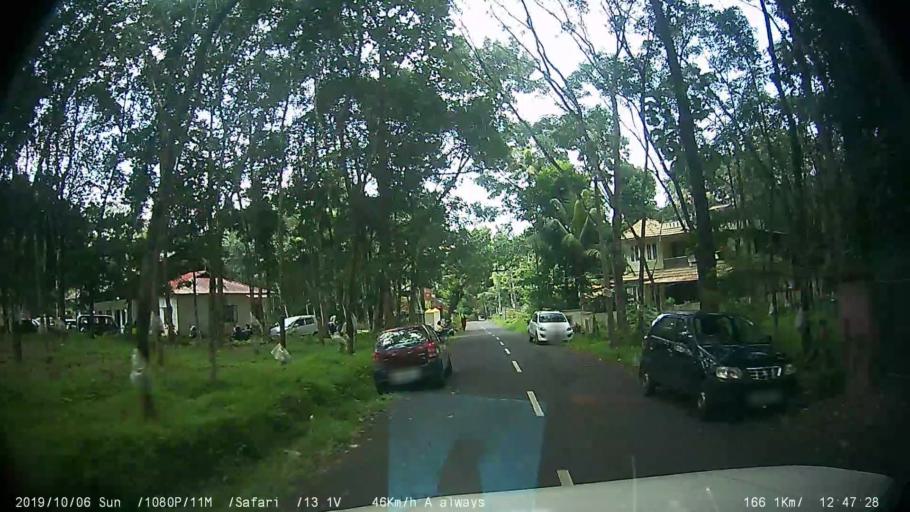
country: IN
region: Kerala
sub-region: Kottayam
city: Palackattumala
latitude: 9.7748
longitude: 76.6016
